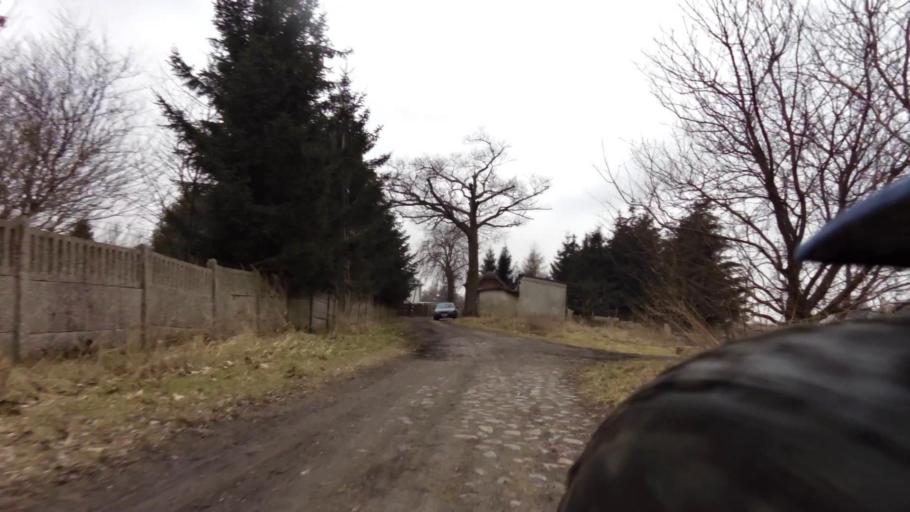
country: PL
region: West Pomeranian Voivodeship
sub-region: Powiat walecki
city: Walcz
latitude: 53.2313
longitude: 16.4539
